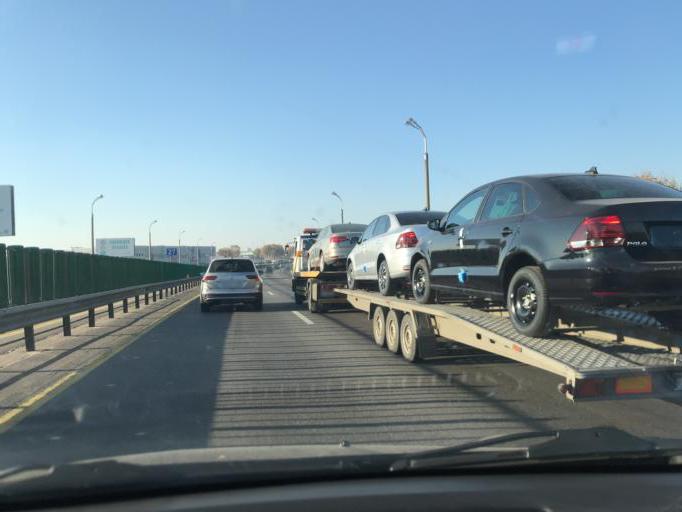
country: BY
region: Minsk
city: Malinovka
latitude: 53.8473
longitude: 27.4418
